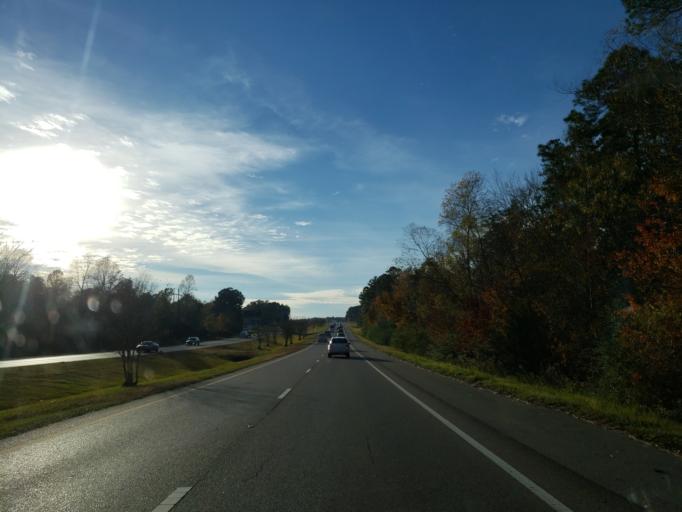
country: US
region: Mississippi
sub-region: Lamar County
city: West Hattiesburg
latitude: 31.3140
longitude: -89.4607
